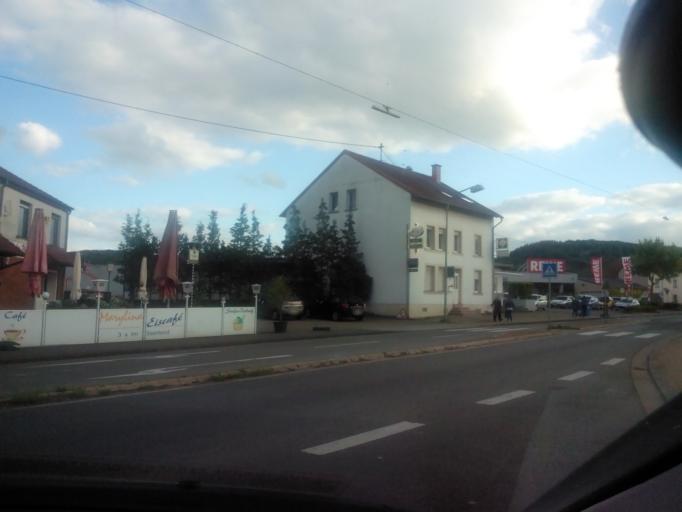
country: DE
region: Saarland
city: Rehlingen-Siersburg
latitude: 49.3651
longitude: 6.6680
